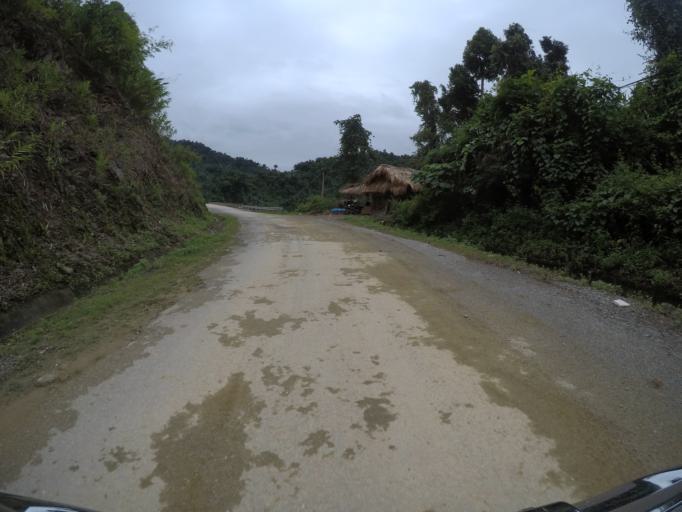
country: VN
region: Quang Nam
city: Thanh My
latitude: 15.6537
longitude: 107.6216
